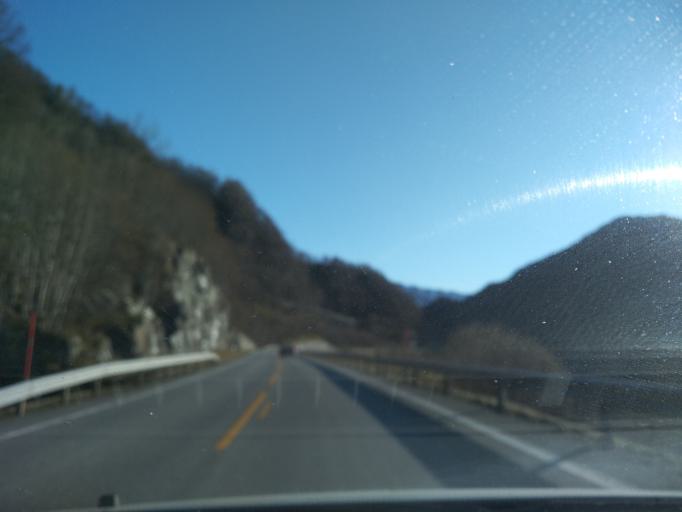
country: NO
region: Hordaland
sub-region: Etne
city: Etne
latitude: 59.7445
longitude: 6.1228
